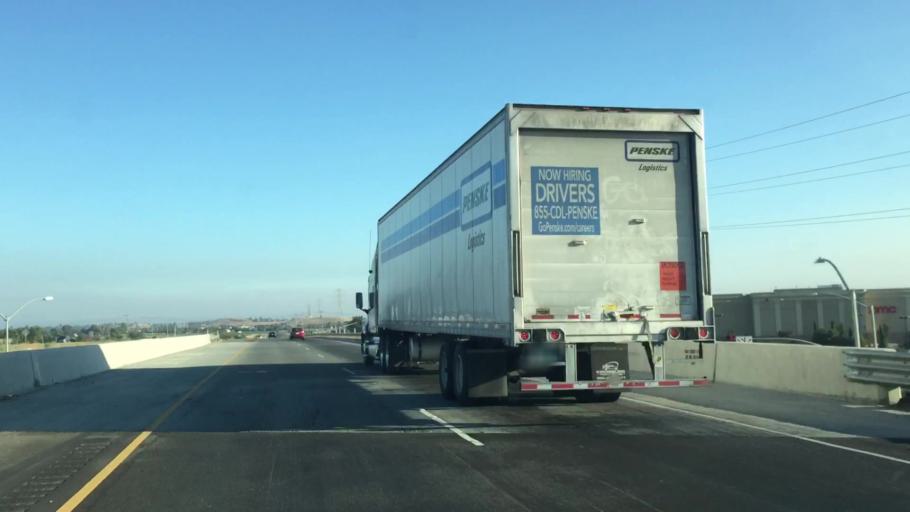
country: US
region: California
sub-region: Contra Costa County
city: Brentwood
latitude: 37.9433
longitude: -121.7413
